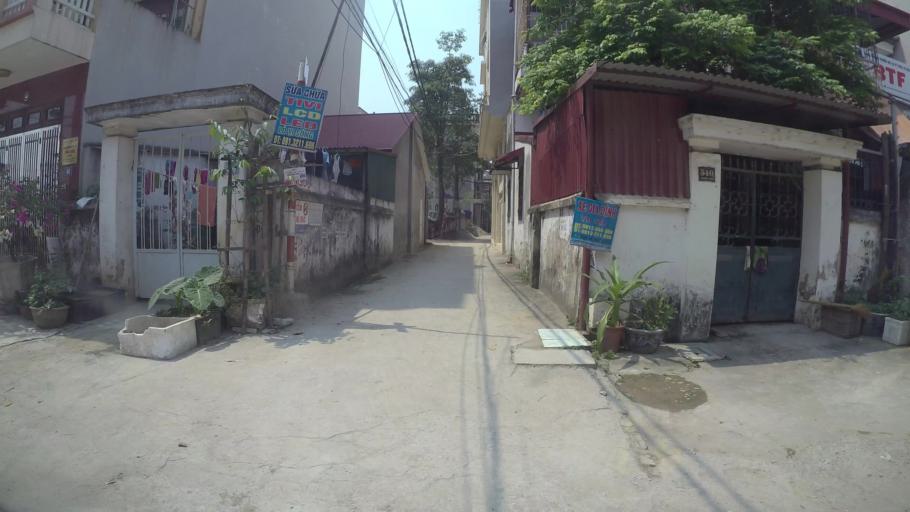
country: VN
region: Ha Noi
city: Ha Dong
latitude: 20.9857
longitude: 105.7635
